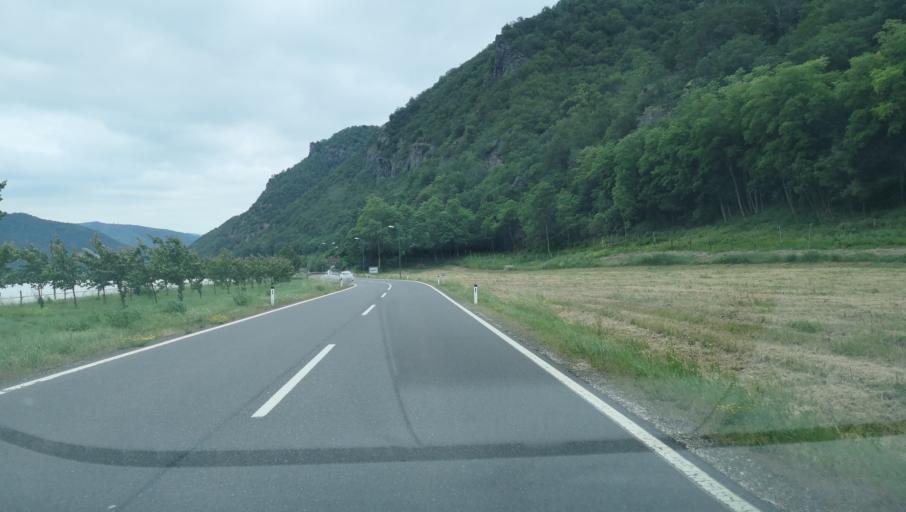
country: AT
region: Lower Austria
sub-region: Politischer Bezirk Krems
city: Aggsbach
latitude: 48.3134
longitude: 15.4132
